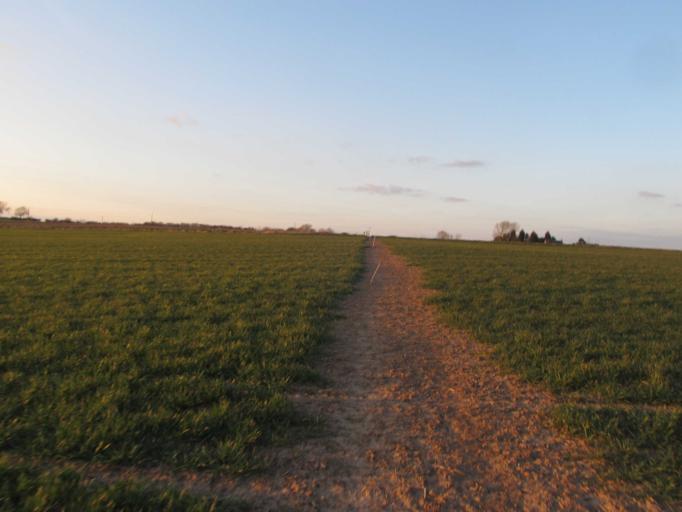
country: GB
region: England
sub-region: Nottinghamshire
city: Misterton
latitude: 53.3995
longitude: -0.8556
